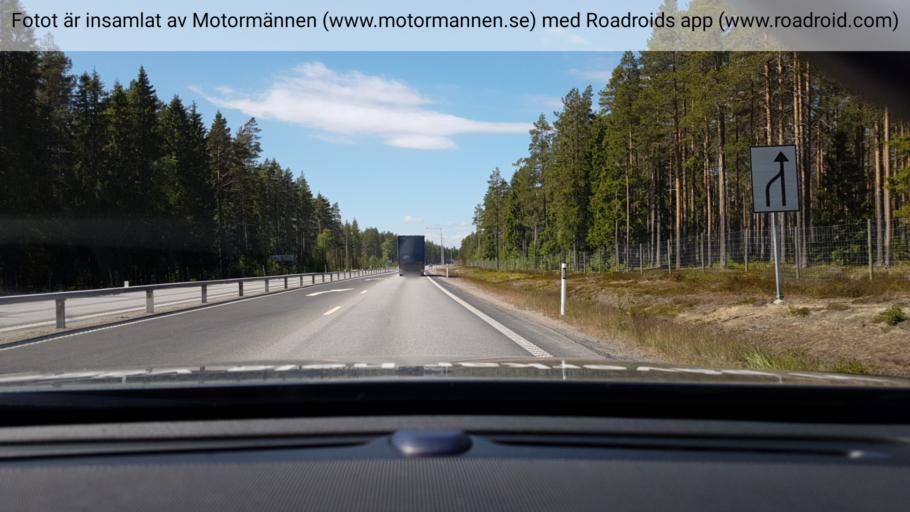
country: SE
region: Vaesterbotten
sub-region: Nordmalings Kommun
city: Nordmaling
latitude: 63.5904
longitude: 19.6918
